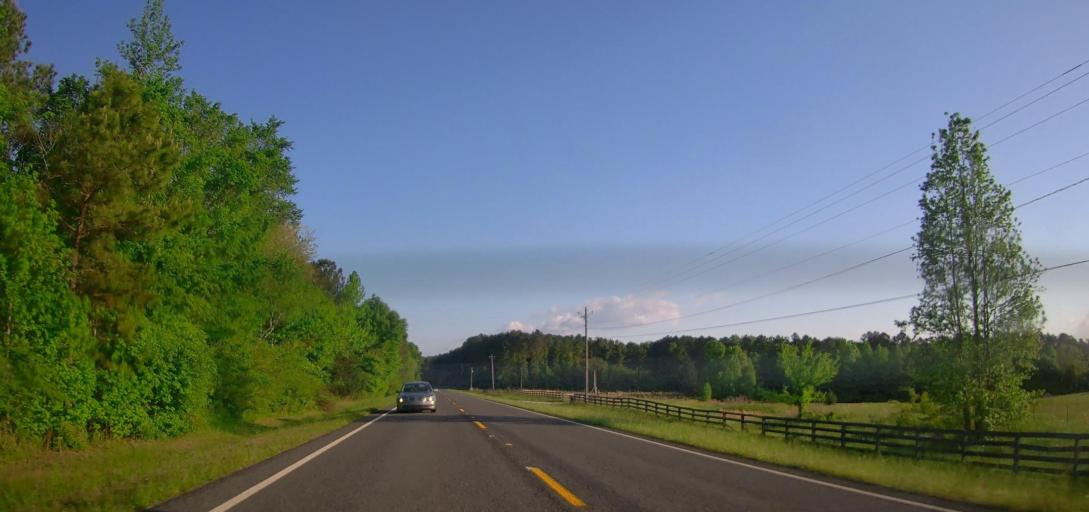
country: US
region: Georgia
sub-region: Jasper County
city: Monticello
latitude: 33.4342
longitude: -83.6196
